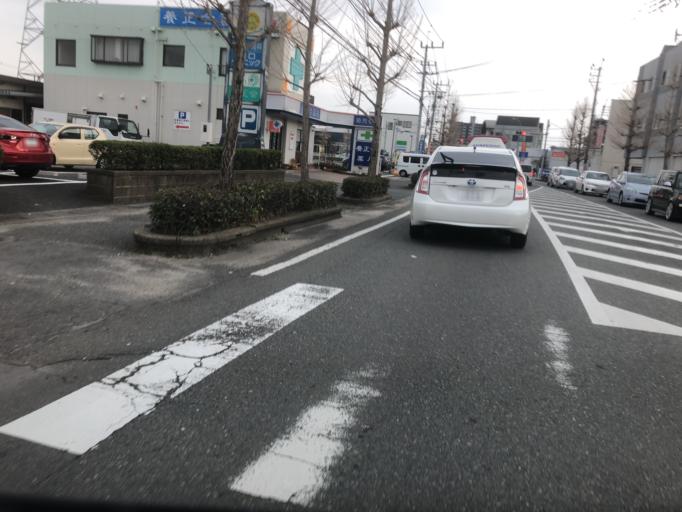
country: JP
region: Saga Prefecture
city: Saga-shi
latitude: 33.2832
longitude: 130.2687
